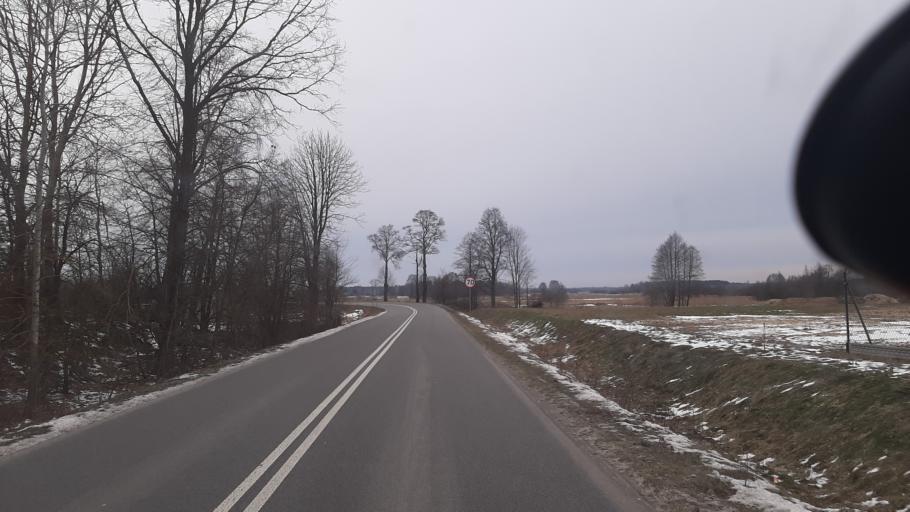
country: PL
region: Lublin Voivodeship
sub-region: Powiat lubartowski
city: Kamionka
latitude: 51.4860
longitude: 22.4471
